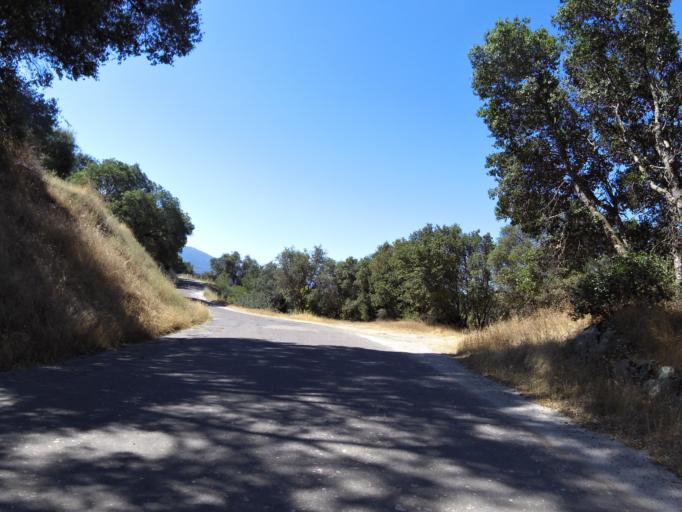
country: US
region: California
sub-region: Fresno County
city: Auberry
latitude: 37.1871
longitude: -119.4642
